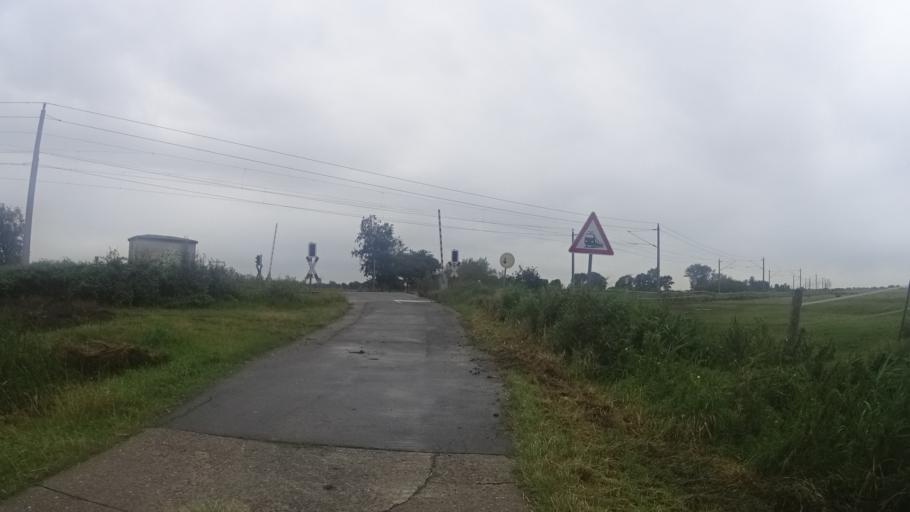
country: DE
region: Schleswig-Holstein
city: Sommerland
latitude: 53.7892
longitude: 9.5374
